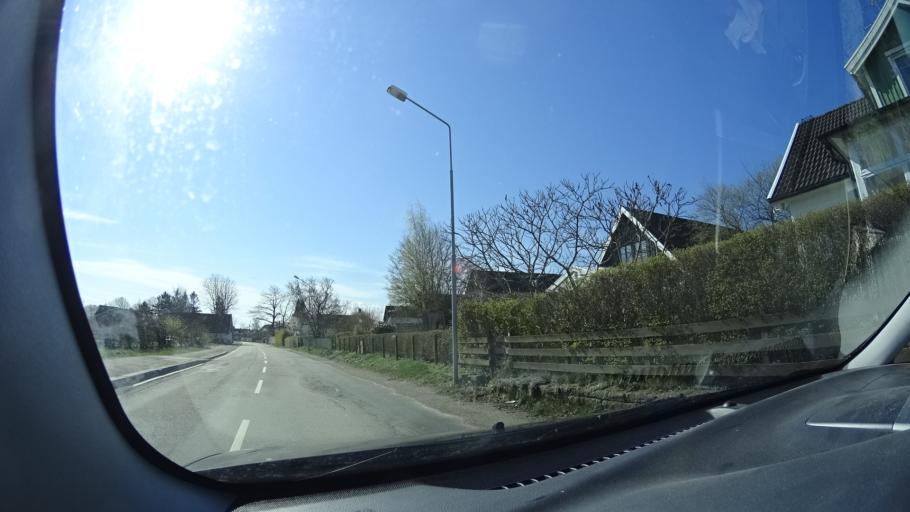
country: SE
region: Skane
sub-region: Hoganas Kommun
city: Hoganas
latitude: 56.2224
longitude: 12.6749
